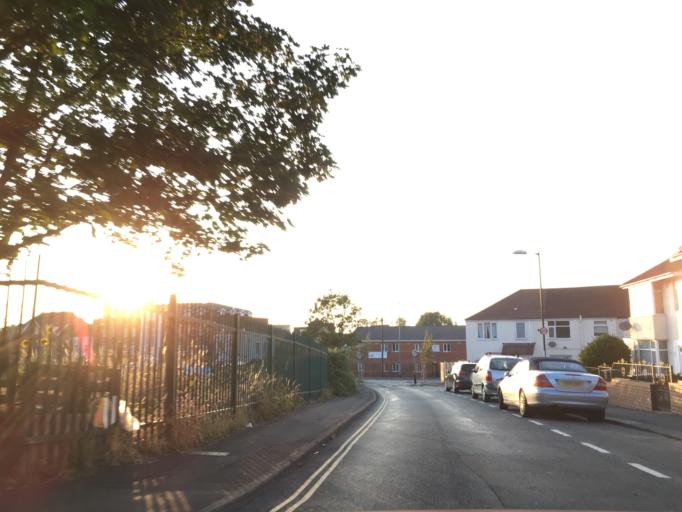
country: GB
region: England
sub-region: South Gloucestershire
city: Kingswood
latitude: 51.4678
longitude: -2.5330
